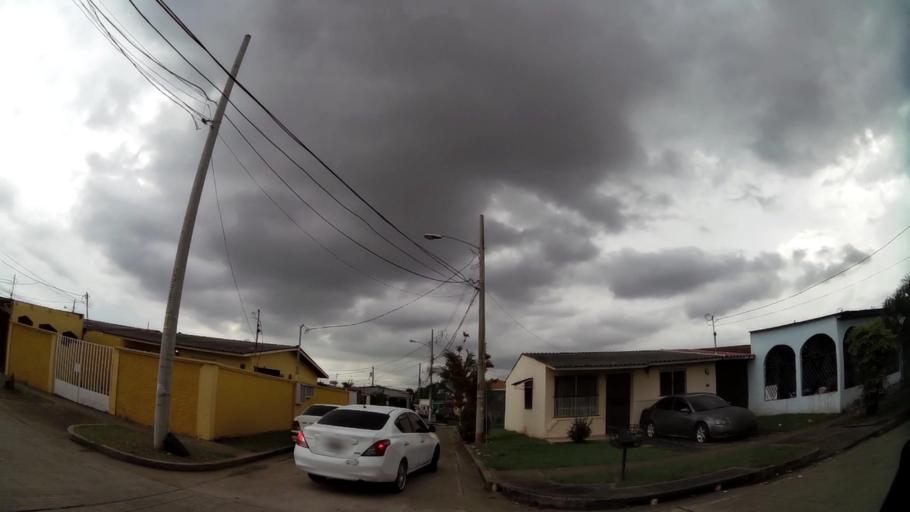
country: PA
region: Panama
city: Tocumen
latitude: 9.0484
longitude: -79.4110
